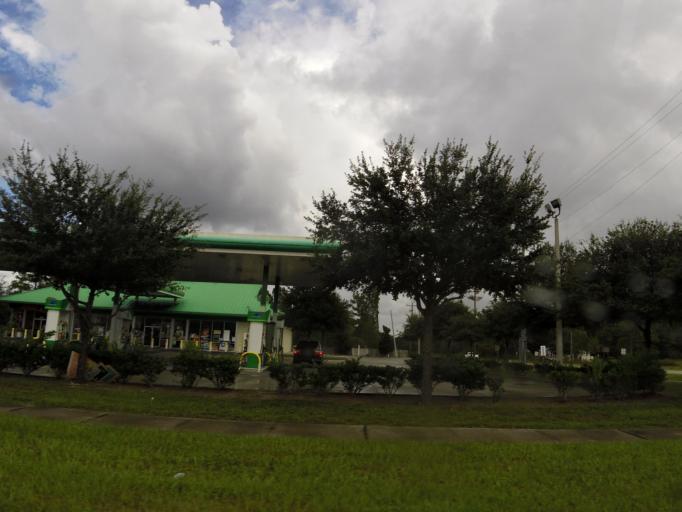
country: US
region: Florida
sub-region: Clay County
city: Middleburg
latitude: 30.0882
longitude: -81.9448
